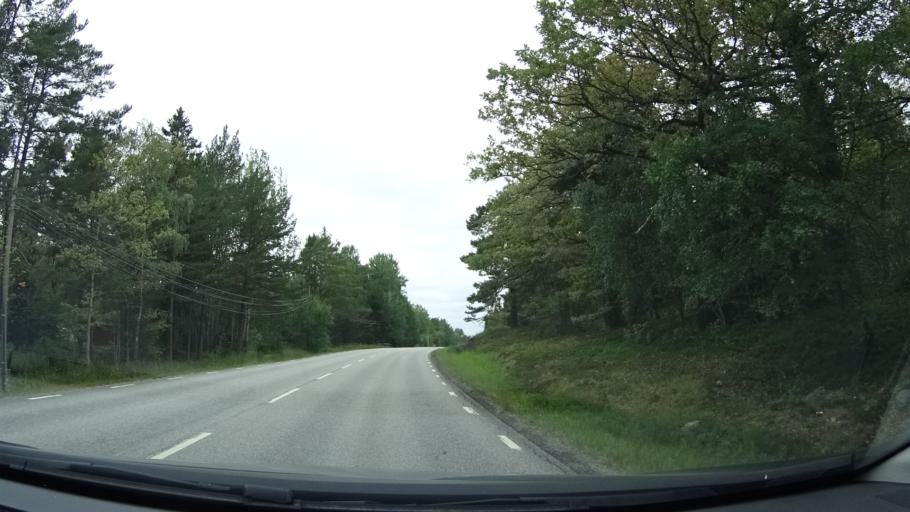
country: SE
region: Stockholm
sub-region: Varmdo Kommun
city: Hemmesta
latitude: 59.3412
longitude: 18.4831
